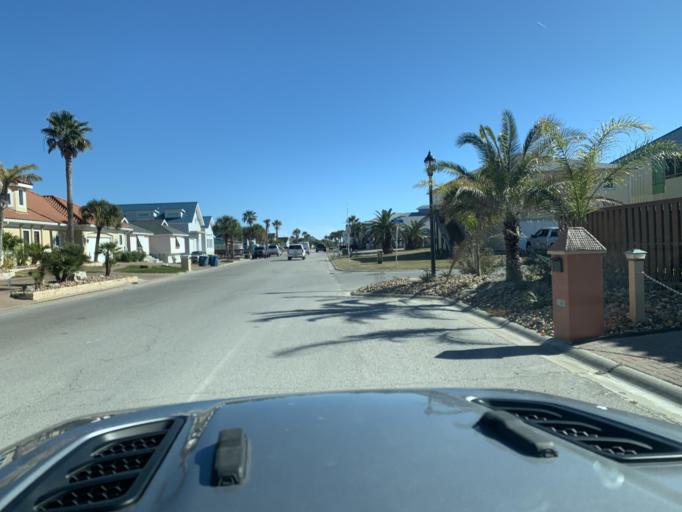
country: US
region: Texas
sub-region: Aransas County
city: Fulton
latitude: 28.0488
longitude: -97.0300
